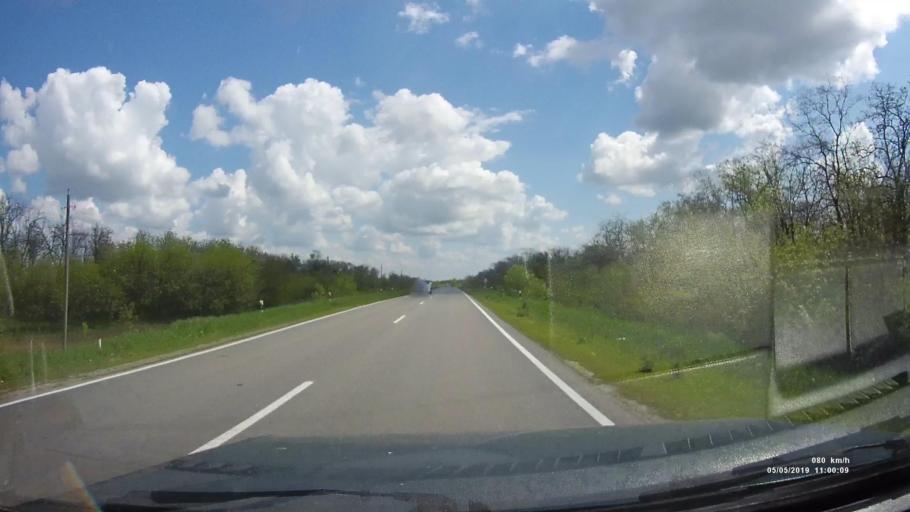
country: RU
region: Rostov
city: Ust'-Donetskiy
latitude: 47.6727
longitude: 40.8807
